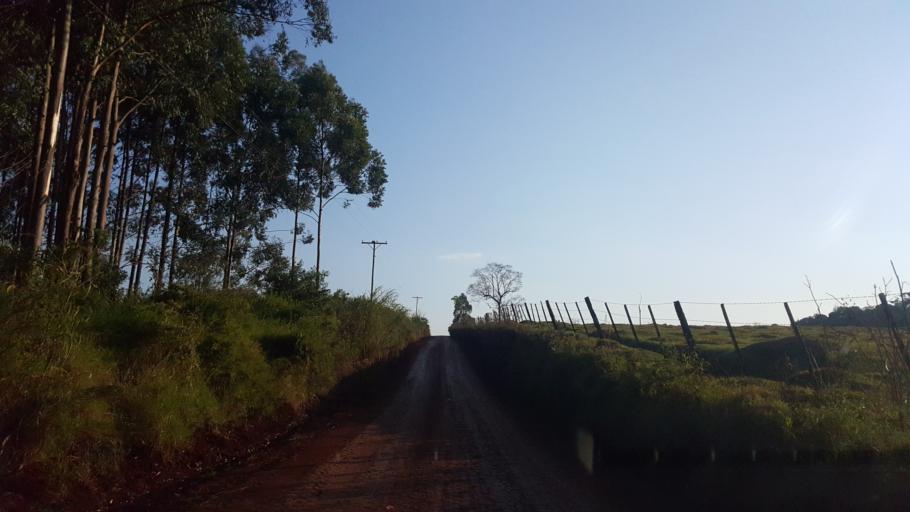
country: AR
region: Misiones
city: Capiovi
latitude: -26.9094
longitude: -55.0508
